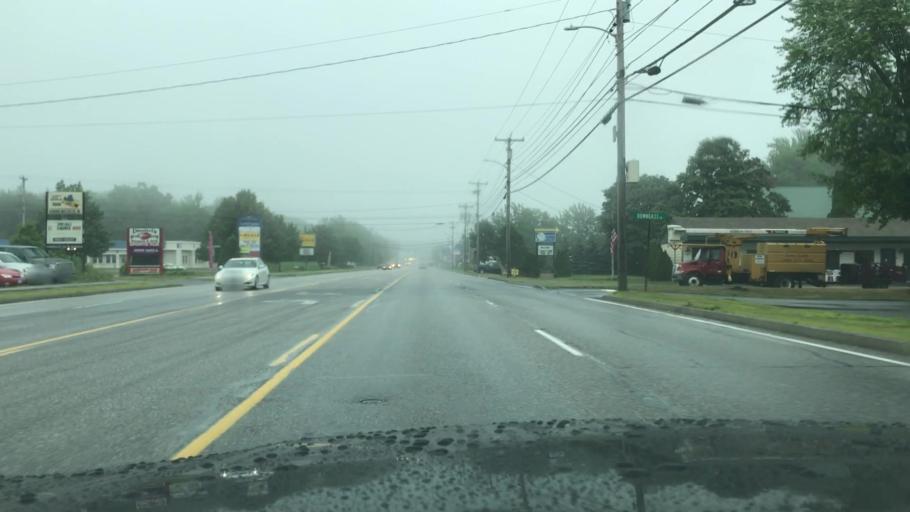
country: US
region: Maine
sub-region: Cumberland County
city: Scarborough
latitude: 43.5937
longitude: -70.3282
